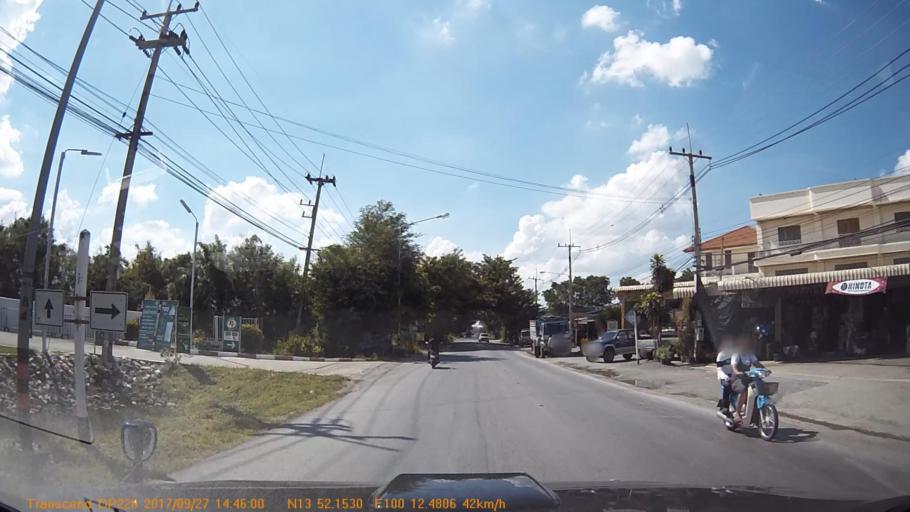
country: TH
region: Nakhon Pathom
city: Nakhon Chai Si
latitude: 13.8690
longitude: 100.2081
